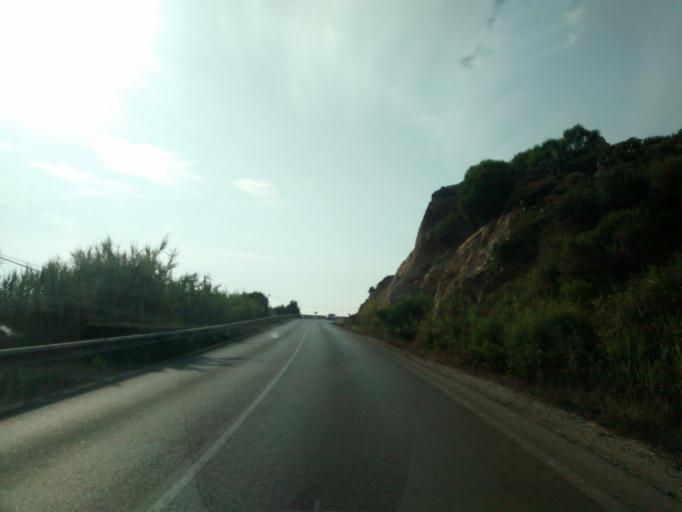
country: ES
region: Andalusia
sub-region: Provincia de Cadiz
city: Zahara de los Atunes
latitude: 36.1388
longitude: -5.8491
